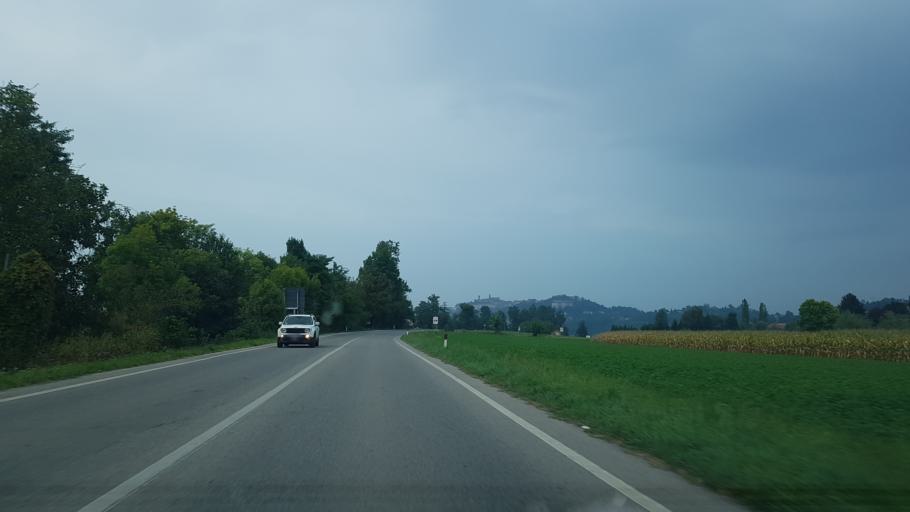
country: IT
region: Piedmont
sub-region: Provincia di Cuneo
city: Mondovi
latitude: 44.3696
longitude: 7.8000
